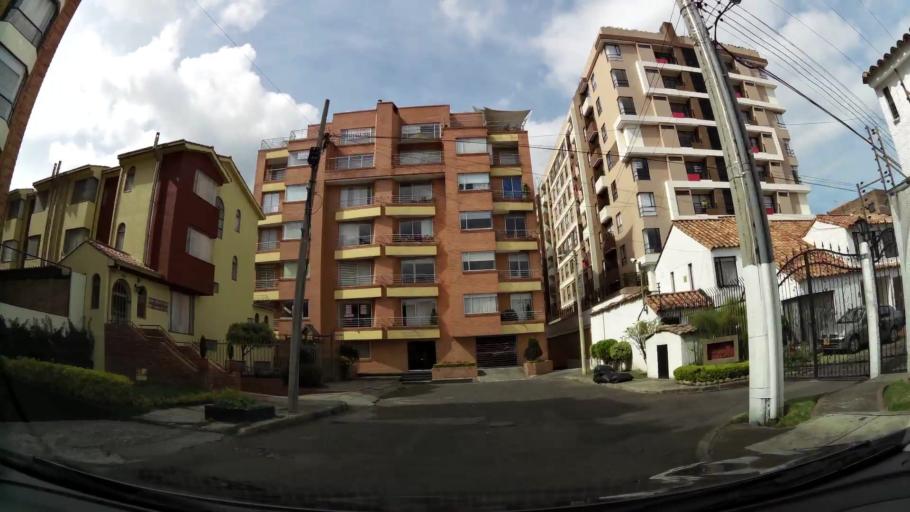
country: CO
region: Bogota D.C.
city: Barrio San Luis
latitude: 4.7243
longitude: -74.0311
